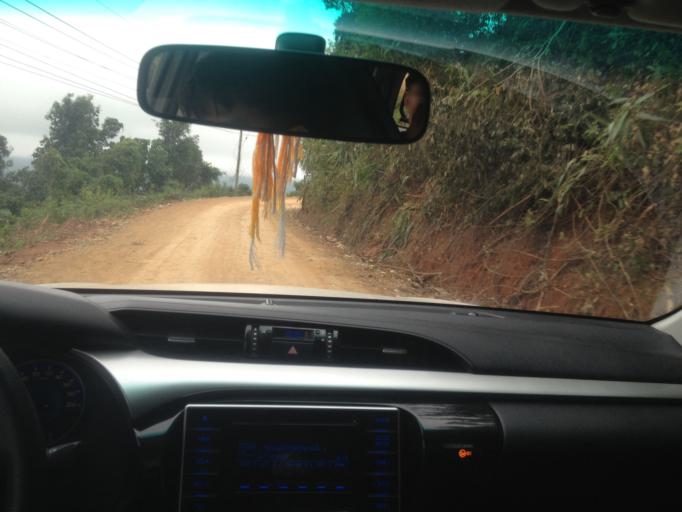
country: TH
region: Nan
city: Chaloem Phra Kiat
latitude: 19.9937
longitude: 101.1360
